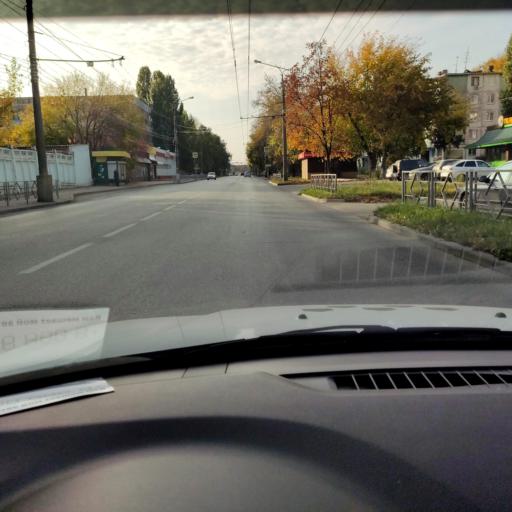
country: RU
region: Samara
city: Tol'yatti
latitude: 53.5131
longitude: 49.4295
